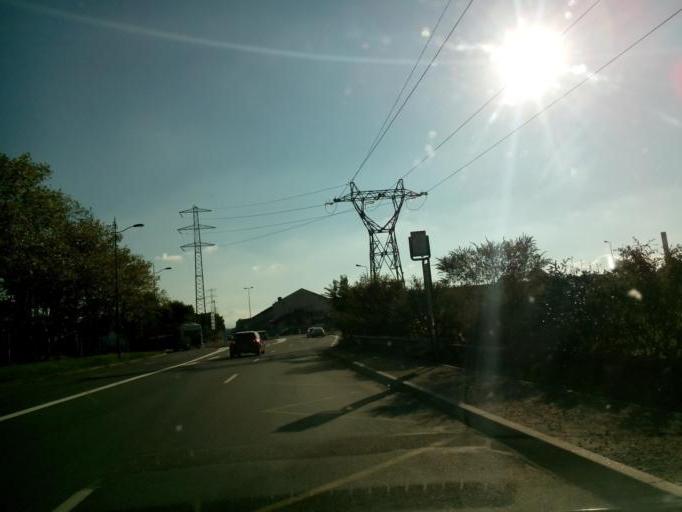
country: FR
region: Rhone-Alpes
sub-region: Departement du Rhone
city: Bron
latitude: 45.7121
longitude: 4.9030
